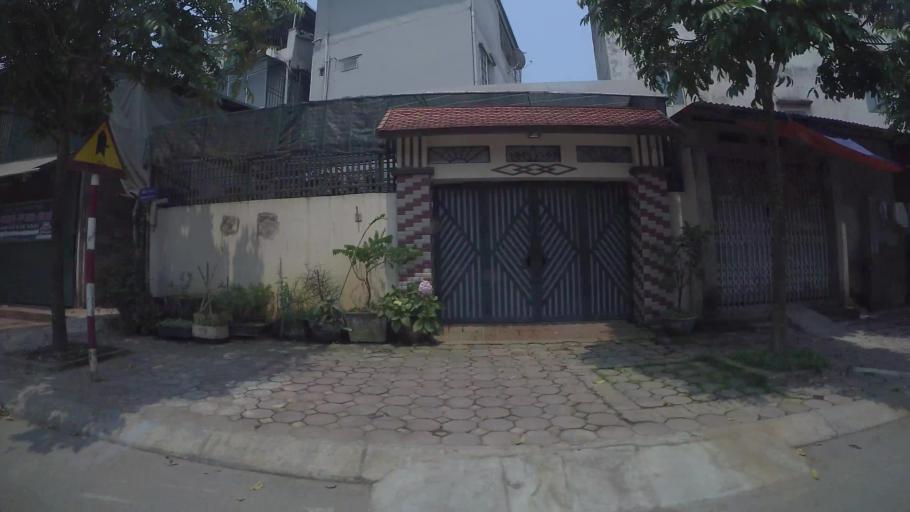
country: VN
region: Ha Noi
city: Van Dien
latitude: 20.9511
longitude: 105.8367
